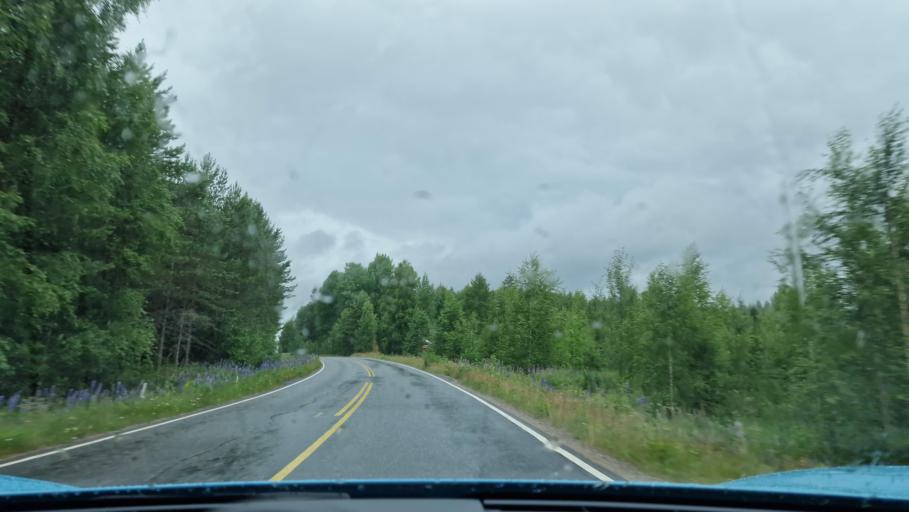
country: FI
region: Southern Ostrobothnia
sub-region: Jaerviseutu
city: Soini
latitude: 62.8015
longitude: 24.3712
